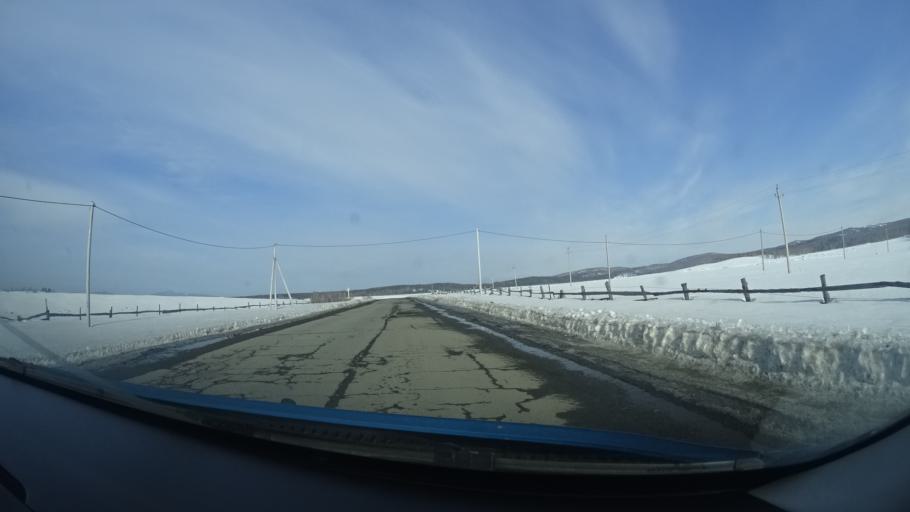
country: RU
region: Bashkortostan
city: Lomovka
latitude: 53.8041
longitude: 58.2693
